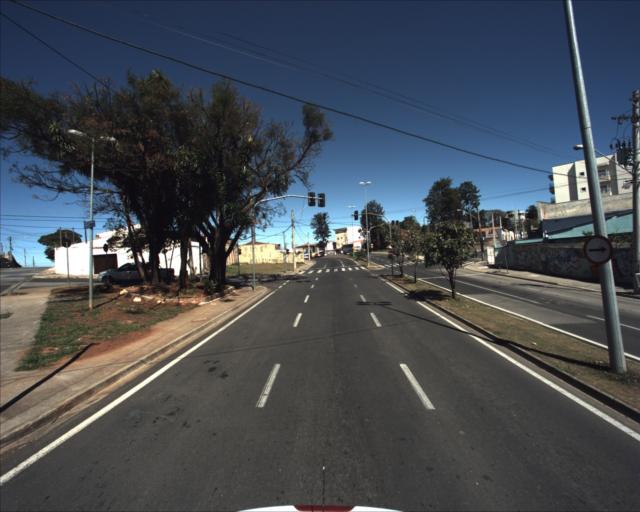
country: BR
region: Sao Paulo
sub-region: Sorocaba
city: Sorocaba
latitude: -23.4980
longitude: -47.4821
